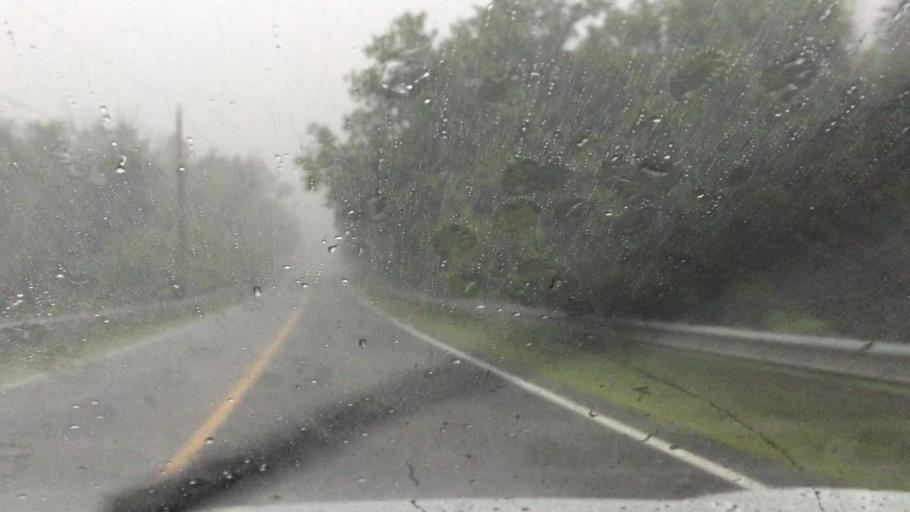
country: CA
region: Ontario
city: Markham
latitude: 43.8602
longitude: -79.2046
